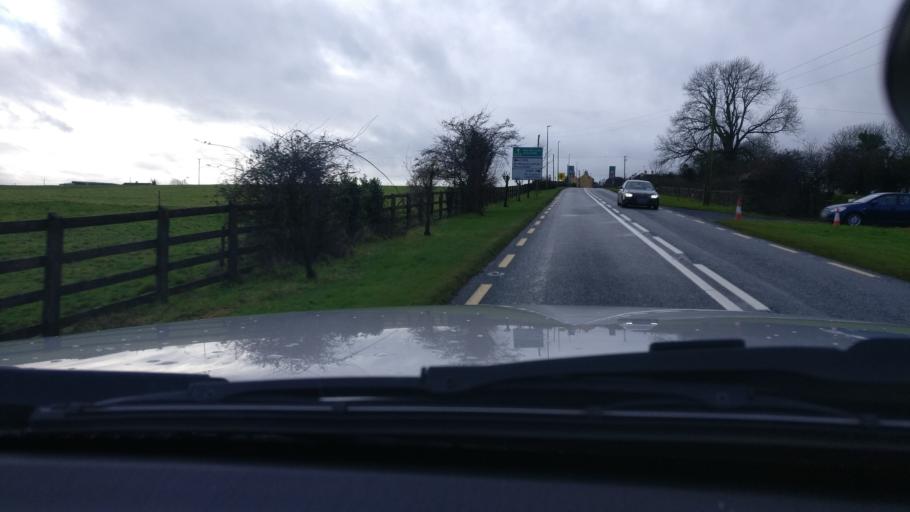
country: IE
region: Leinster
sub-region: An Iarmhi
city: Moate
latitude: 53.6343
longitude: -7.6825
